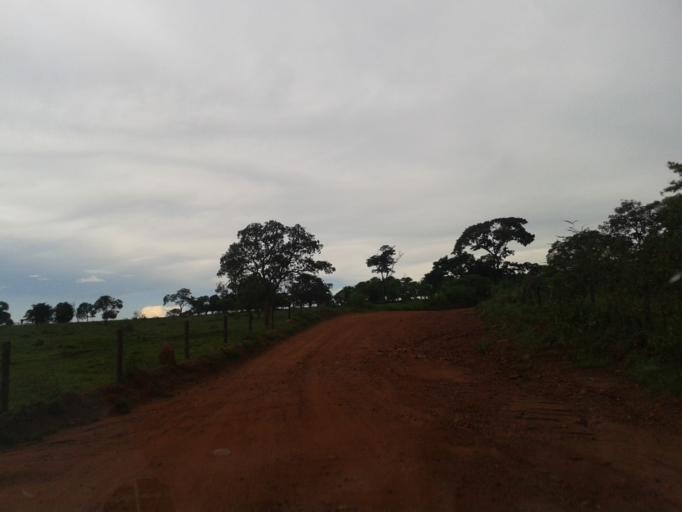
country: BR
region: Minas Gerais
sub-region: Santa Vitoria
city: Santa Vitoria
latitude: -19.1106
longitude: -50.5201
